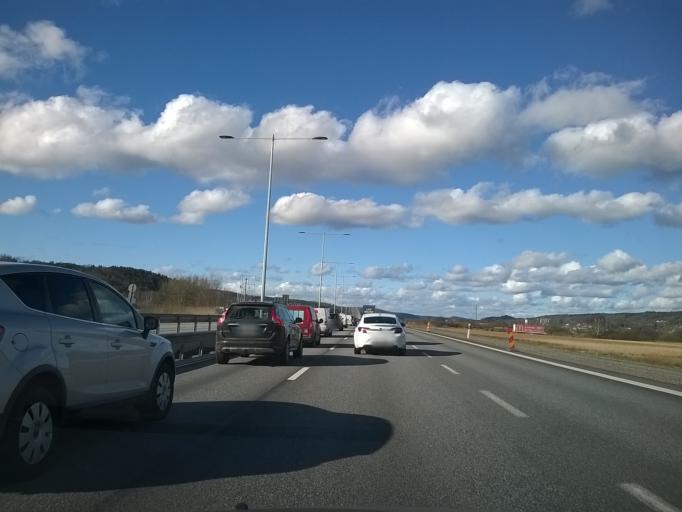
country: SE
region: Vaestra Goetaland
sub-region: Goteborg
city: Gardsten
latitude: 57.8040
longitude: 12.0078
